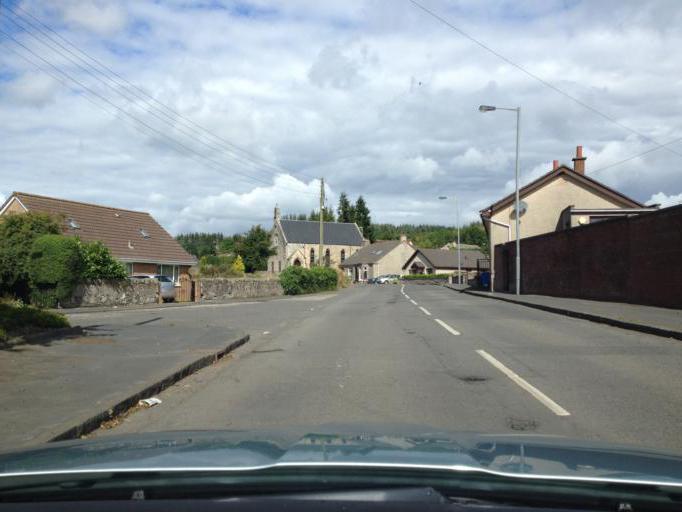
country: GB
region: Scotland
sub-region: Falkirk
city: Polmont
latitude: 55.9362
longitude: -3.7449
